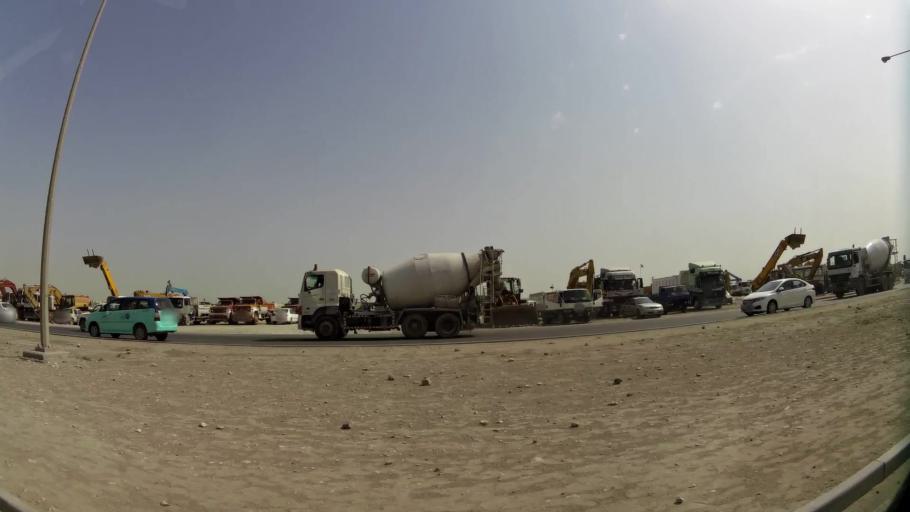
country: QA
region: Al Wakrah
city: Al Wukayr
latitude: 25.1787
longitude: 51.4649
